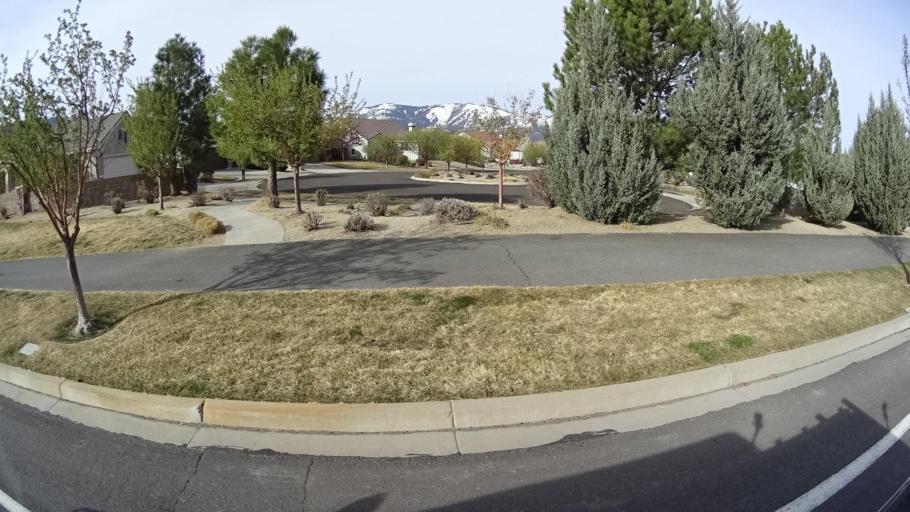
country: US
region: Nevada
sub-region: Washoe County
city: Mogul
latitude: 39.5270
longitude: -119.9484
